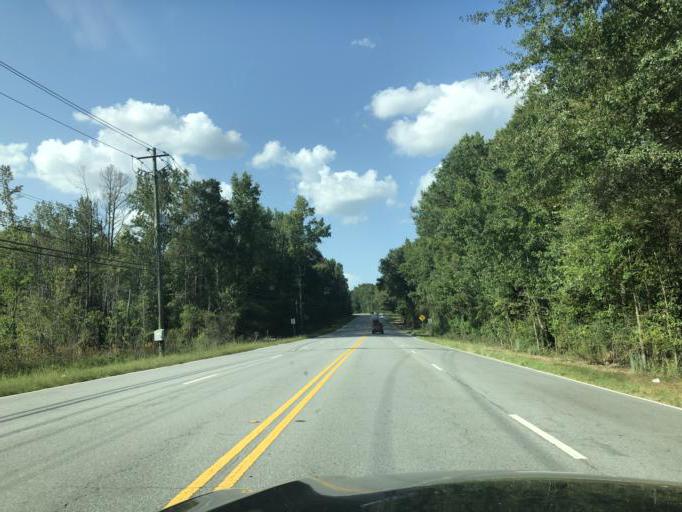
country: US
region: Georgia
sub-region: Muscogee County
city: Columbus
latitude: 32.5055
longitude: -84.8918
